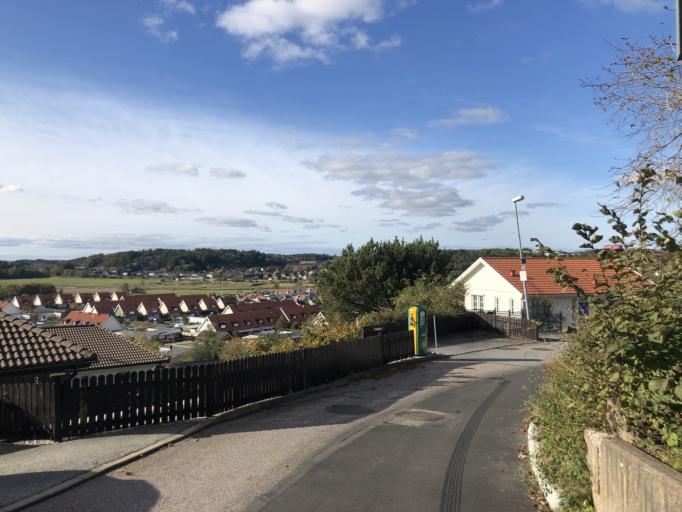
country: SE
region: Vaestra Goetaland
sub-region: Goteborg
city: Majorna
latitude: 57.6345
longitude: 11.9224
